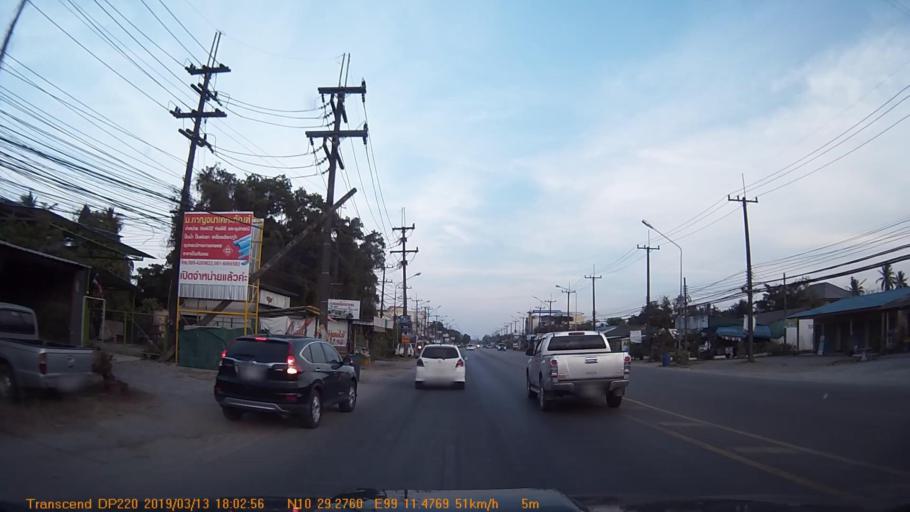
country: TH
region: Chumphon
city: Chumphon
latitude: 10.4878
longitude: 99.1915
